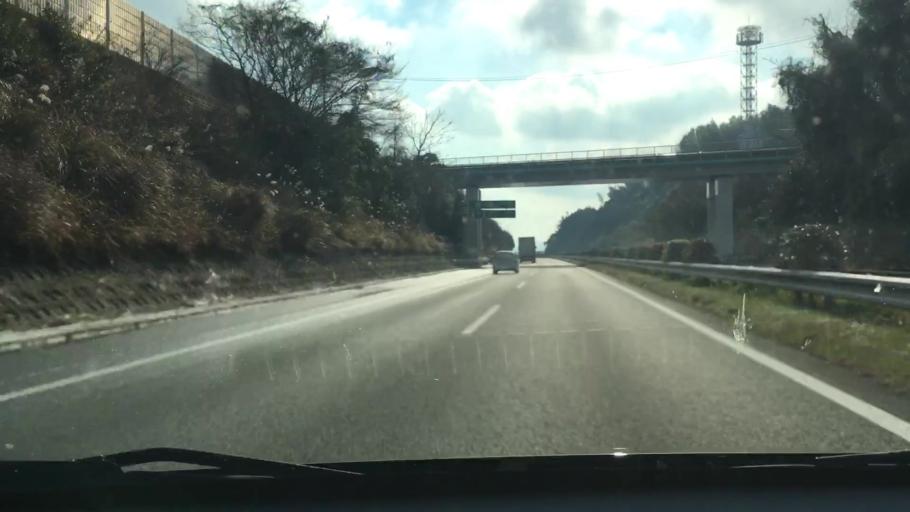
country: JP
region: Kumamoto
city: Kumamoto
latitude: 32.7283
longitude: 130.7737
